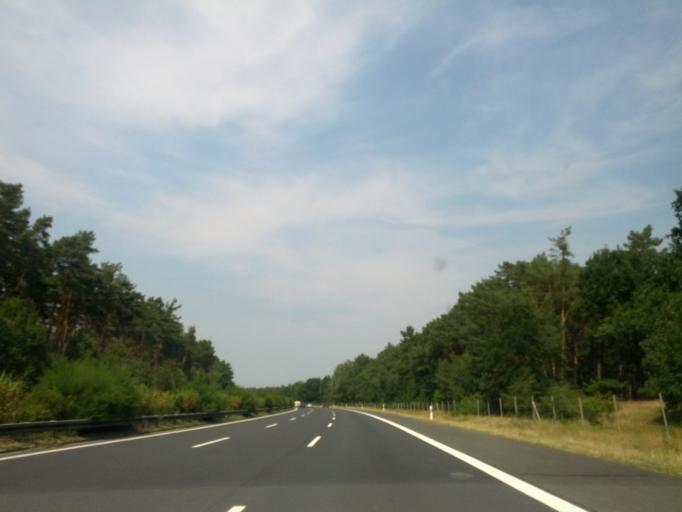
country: DE
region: Brandenburg
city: Beelitz
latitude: 52.2354
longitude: 12.9175
